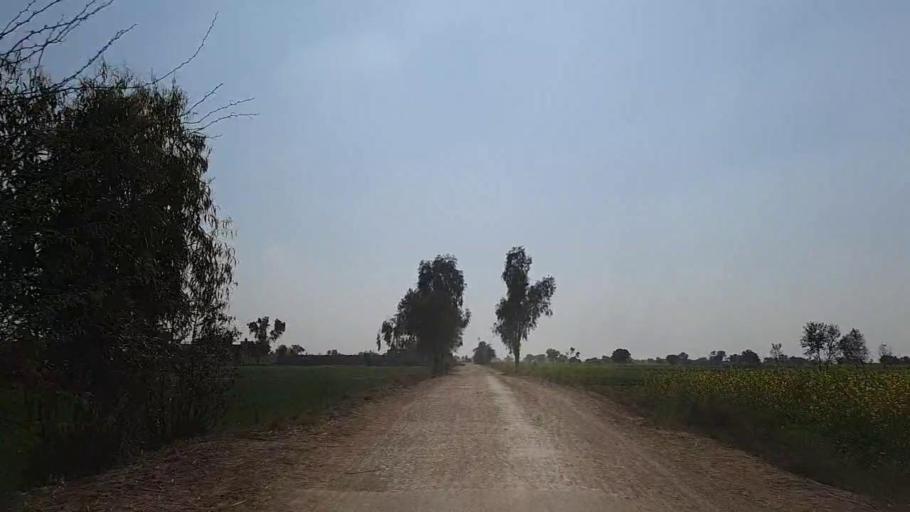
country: PK
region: Sindh
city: Daur
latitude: 26.4582
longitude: 68.2632
